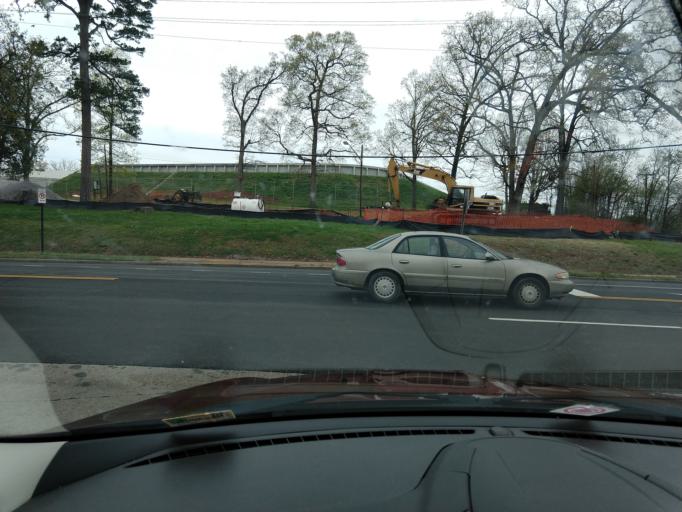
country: US
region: Virginia
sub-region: City of Danville
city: Danville
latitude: 36.5724
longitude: -79.4184
